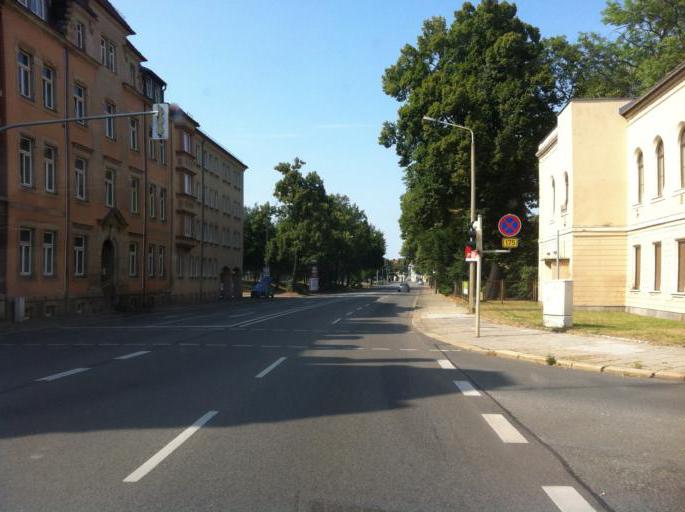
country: DE
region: Saxony
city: Zwickau
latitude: 50.7206
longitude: 12.4881
